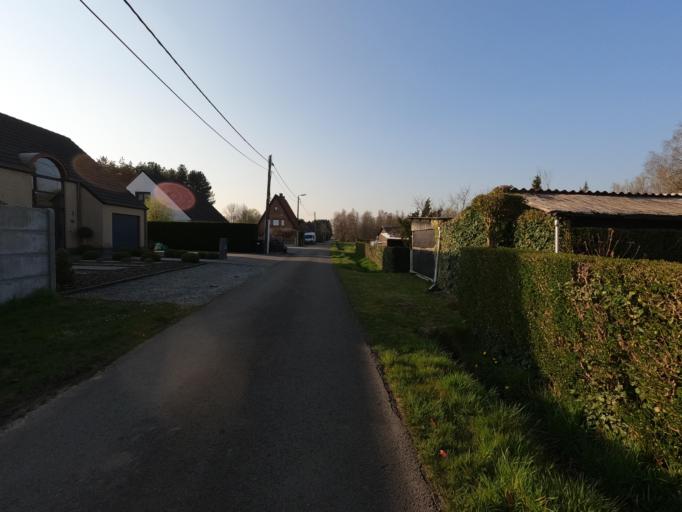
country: BE
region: Flanders
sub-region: Provincie Vlaams-Brabant
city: Aarschot
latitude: 51.0161
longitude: 4.8335
